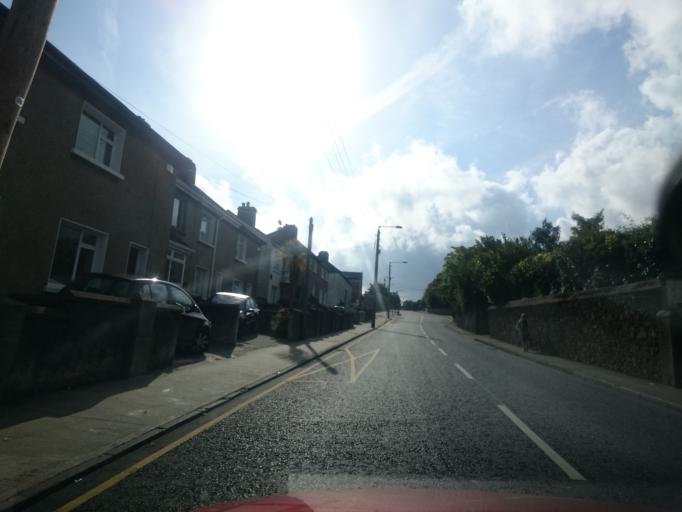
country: IE
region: Leinster
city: Little Bray
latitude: 53.1993
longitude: -6.1100
